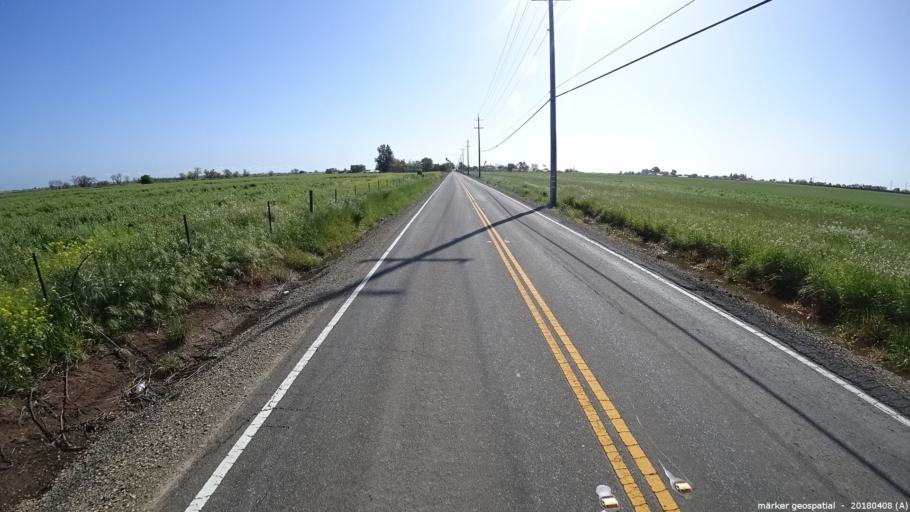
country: US
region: California
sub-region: Sacramento County
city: Laguna
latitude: 38.3723
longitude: -121.4146
